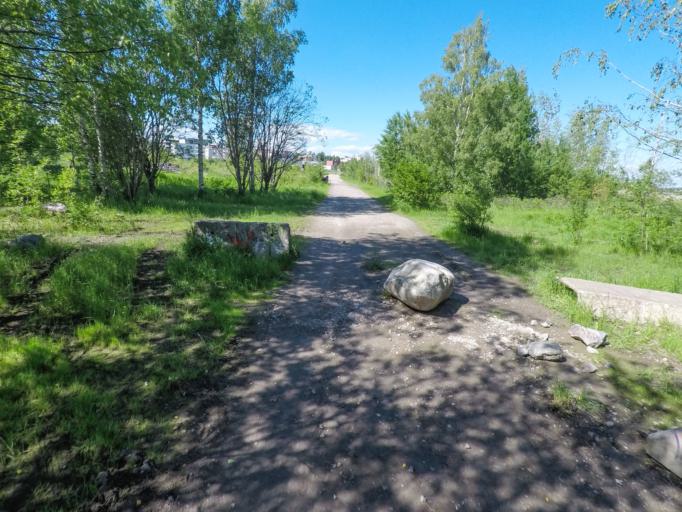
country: FI
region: Uusimaa
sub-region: Helsinki
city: Helsinki
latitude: 60.2010
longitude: 24.9782
